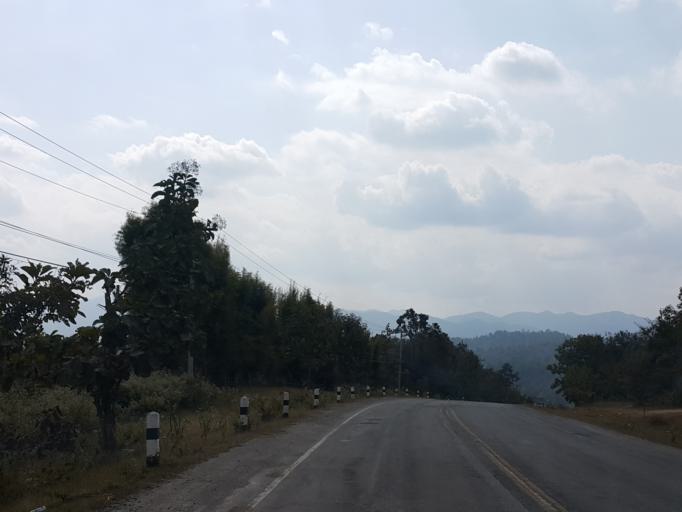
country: TH
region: Chiang Mai
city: Om Koi
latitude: 17.8323
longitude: 98.3680
